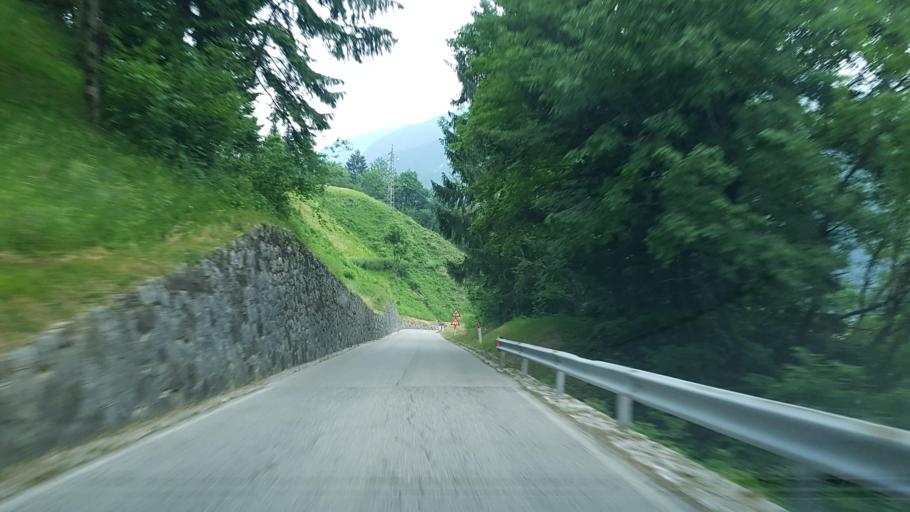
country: IT
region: Friuli Venezia Giulia
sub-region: Provincia di Udine
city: Pontebba
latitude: 46.5131
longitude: 13.2978
